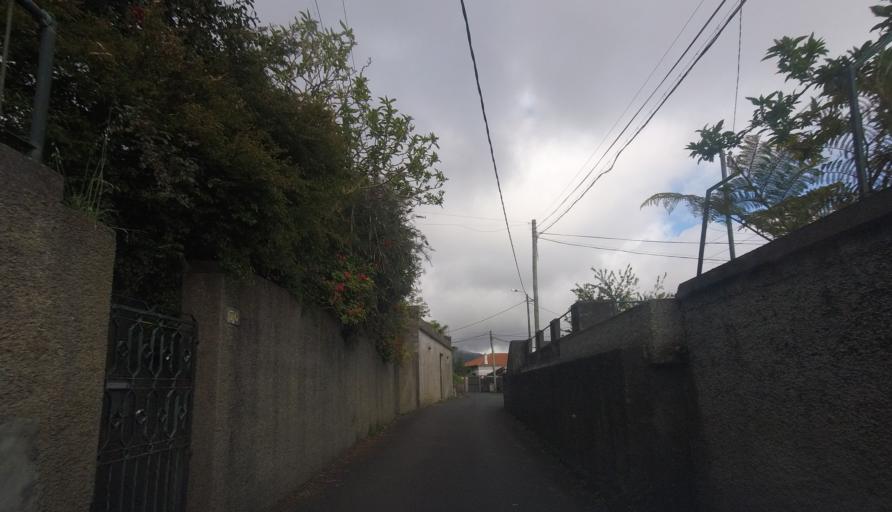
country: PT
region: Madeira
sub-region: Funchal
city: Nossa Senhora do Monte
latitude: 32.6807
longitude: -16.9100
